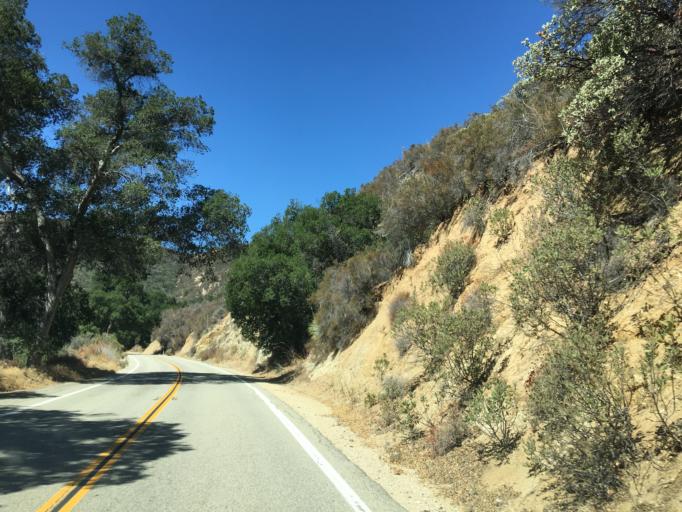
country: US
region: California
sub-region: Los Angeles County
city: Green Valley
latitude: 34.6220
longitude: -118.5579
